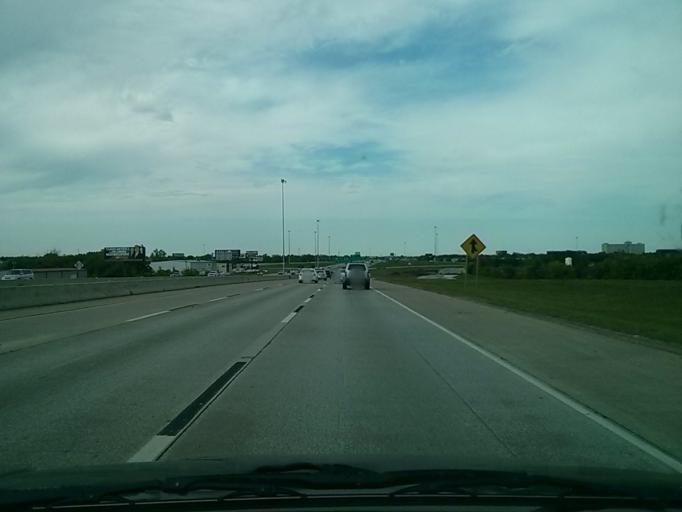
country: US
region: Oklahoma
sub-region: Tulsa County
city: Broken Arrow
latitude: 36.0912
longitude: -95.8588
